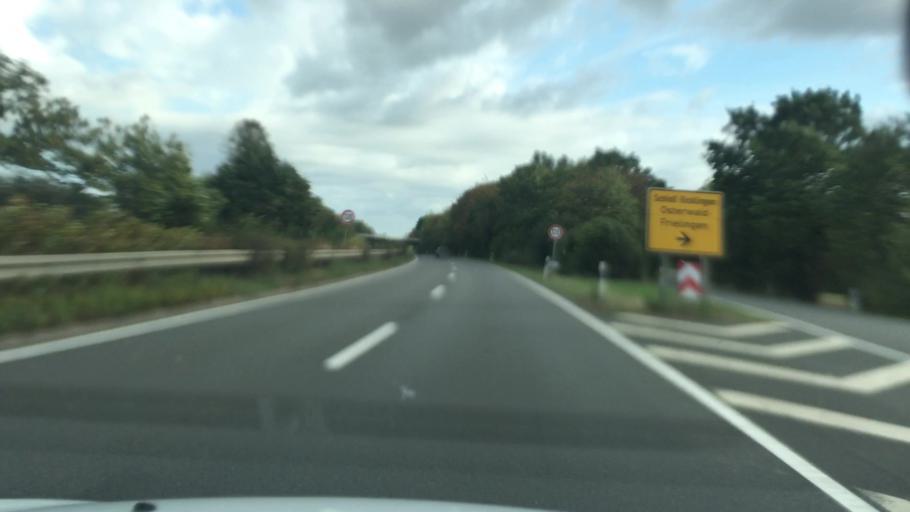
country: DE
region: Lower Saxony
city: Neustadt am Rubenberge
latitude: 52.4663
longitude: 9.5272
